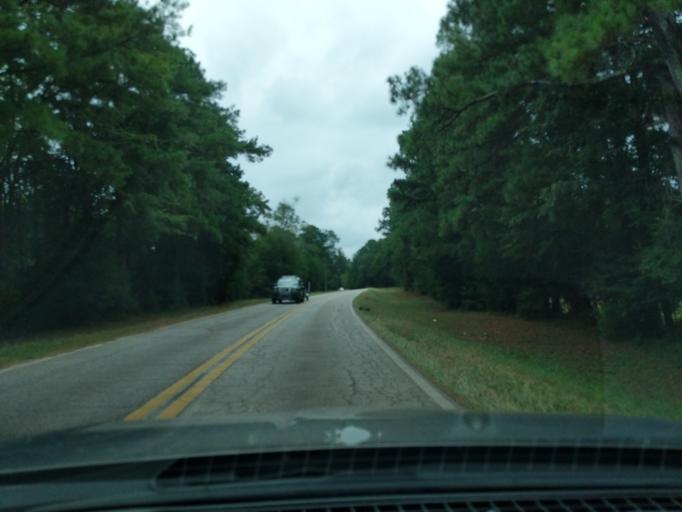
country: US
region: Georgia
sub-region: Columbia County
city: Appling
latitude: 33.5864
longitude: -82.3756
